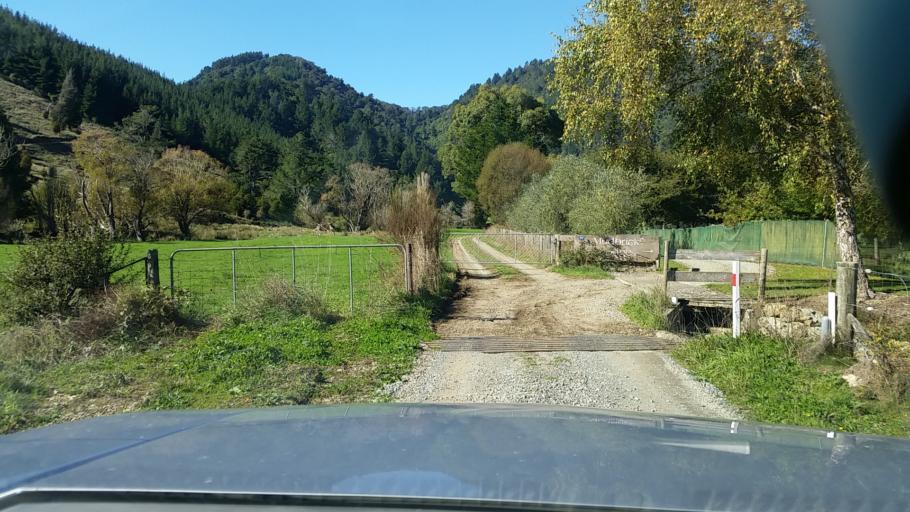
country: NZ
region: Nelson
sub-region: Nelson City
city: Nelson
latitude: -41.2214
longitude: 173.6116
